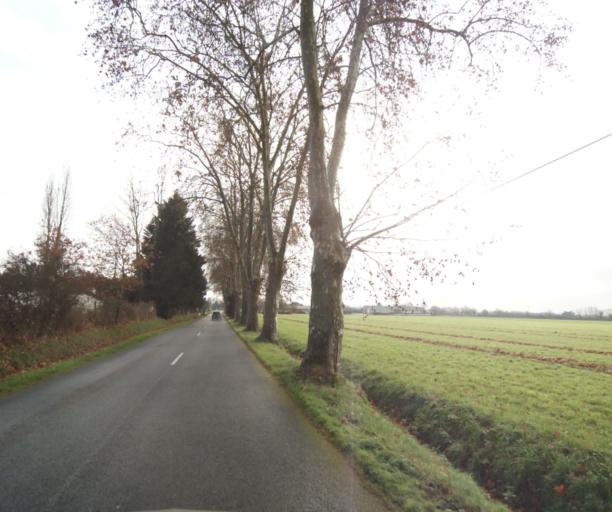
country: FR
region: Midi-Pyrenees
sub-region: Departement de la Haute-Garonne
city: Villemur-sur-Tarn
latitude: 43.8770
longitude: 1.4871
